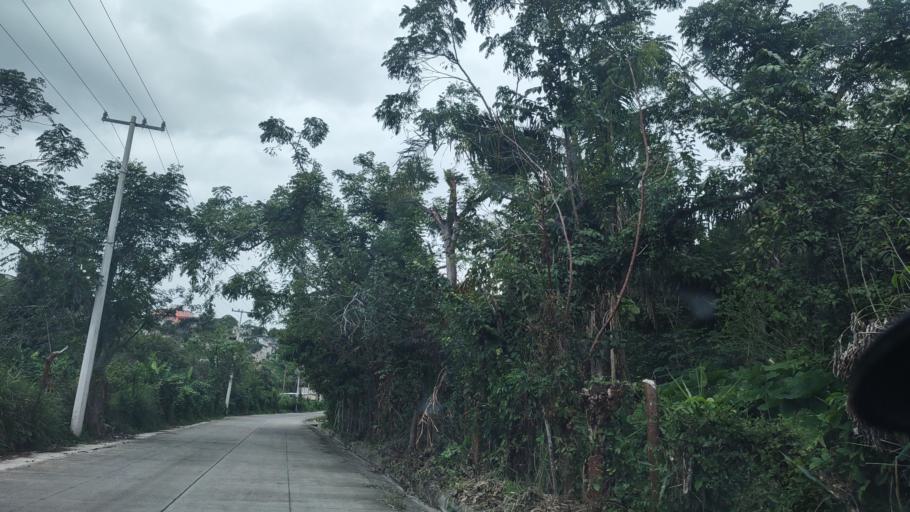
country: MX
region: Veracruz
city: Papantla de Olarte
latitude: 20.4424
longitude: -97.3032
